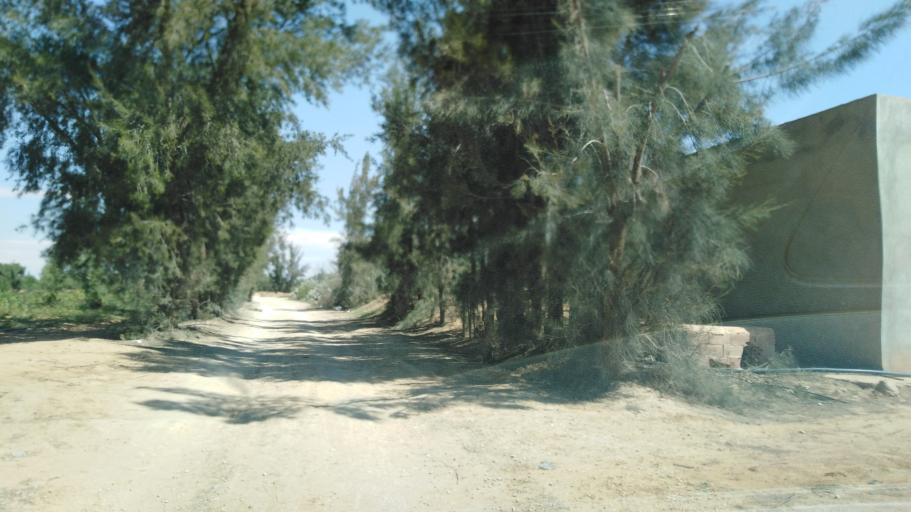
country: TN
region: Safaqis
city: Sfax
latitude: 34.7638
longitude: 10.5284
